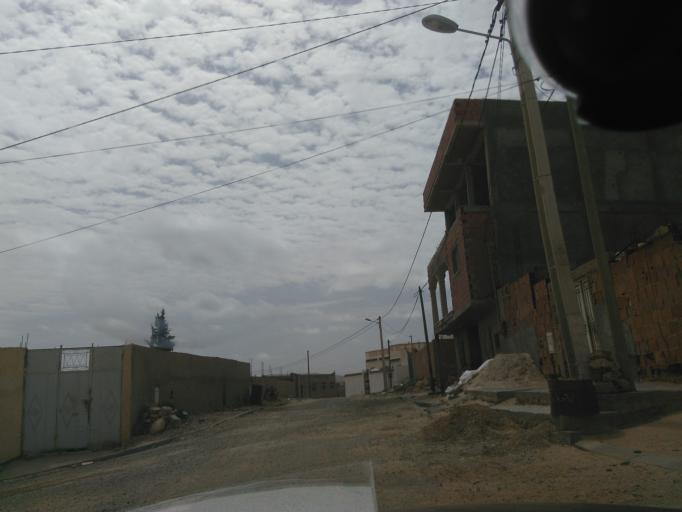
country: TN
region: Tataouine
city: Tataouine
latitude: 32.9465
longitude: 10.4689
